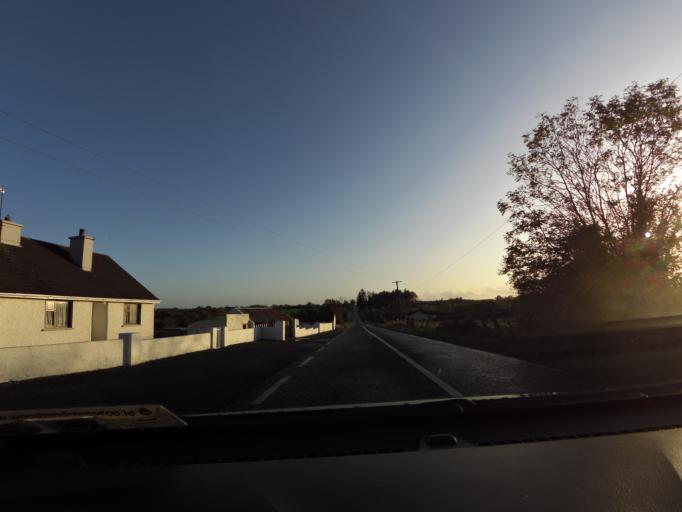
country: IE
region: Connaught
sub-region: Roscommon
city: Castlerea
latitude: 53.7295
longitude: -8.5548
